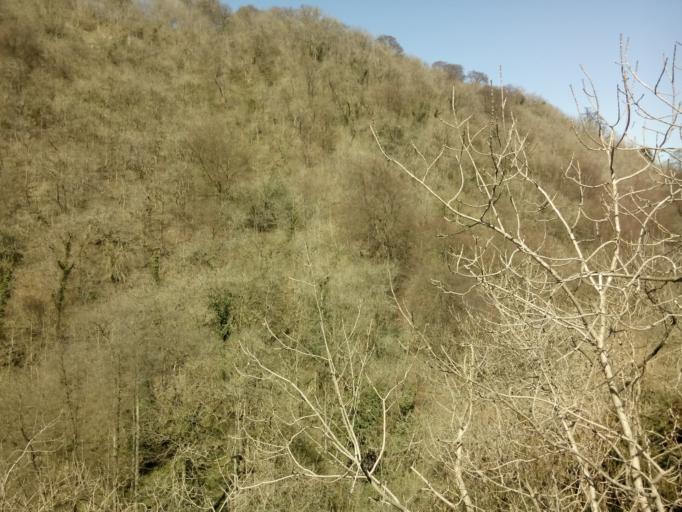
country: GB
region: England
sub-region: Staffordshire
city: Mayfield
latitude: 53.0634
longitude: -1.7845
